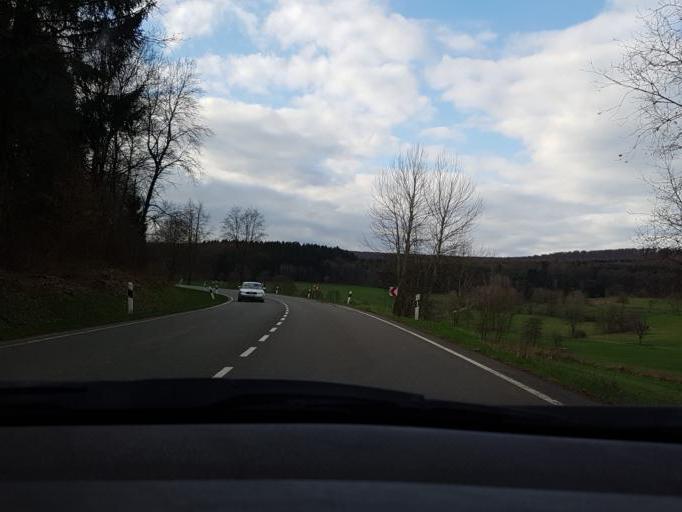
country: DE
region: Lower Saxony
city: Bodenfelde
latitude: 51.7070
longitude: 9.5464
